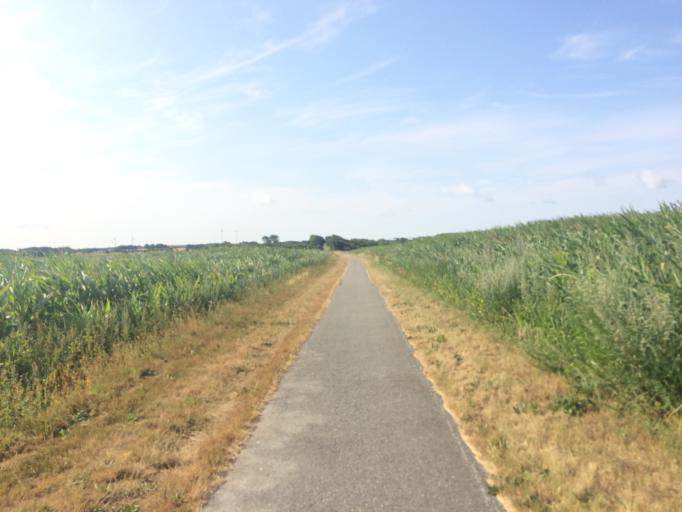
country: DK
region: Central Jutland
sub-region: Holstebro Kommune
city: Vinderup
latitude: 56.6199
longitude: 8.7774
